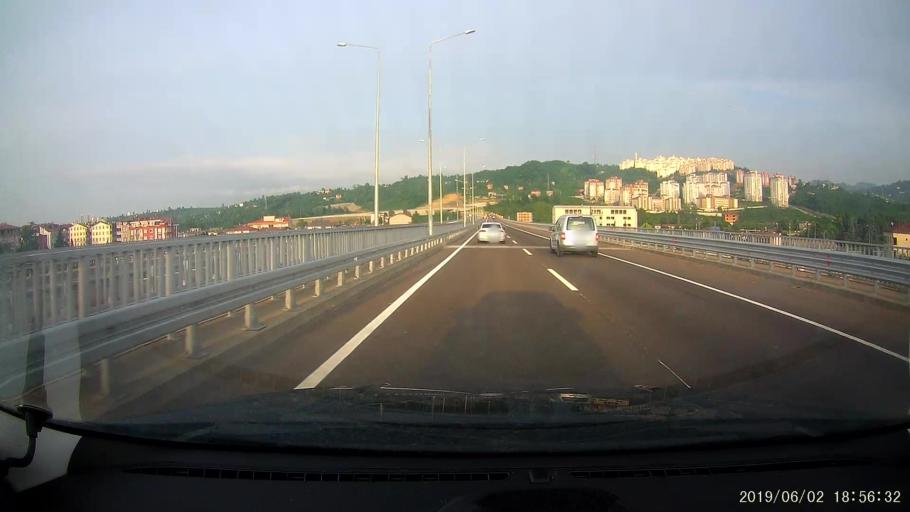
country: TR
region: Ordu
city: Ordu
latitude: 40.9554
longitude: 37.8933
